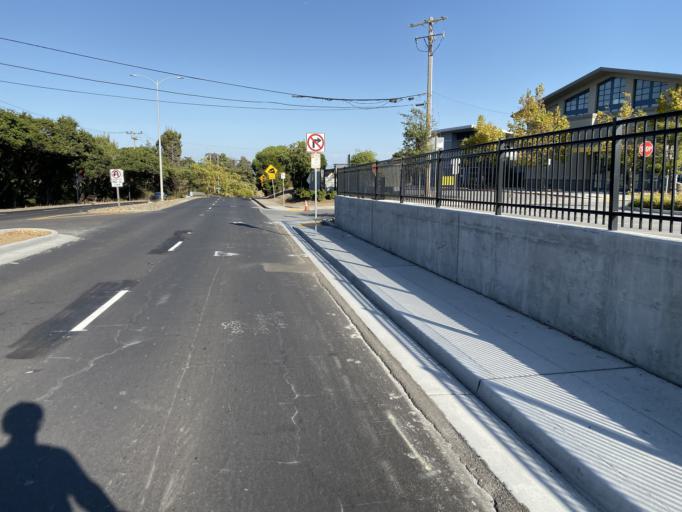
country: US
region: California
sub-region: San Mateo County
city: Highlands-Baywood Park
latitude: 37.5124
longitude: -122.3123
